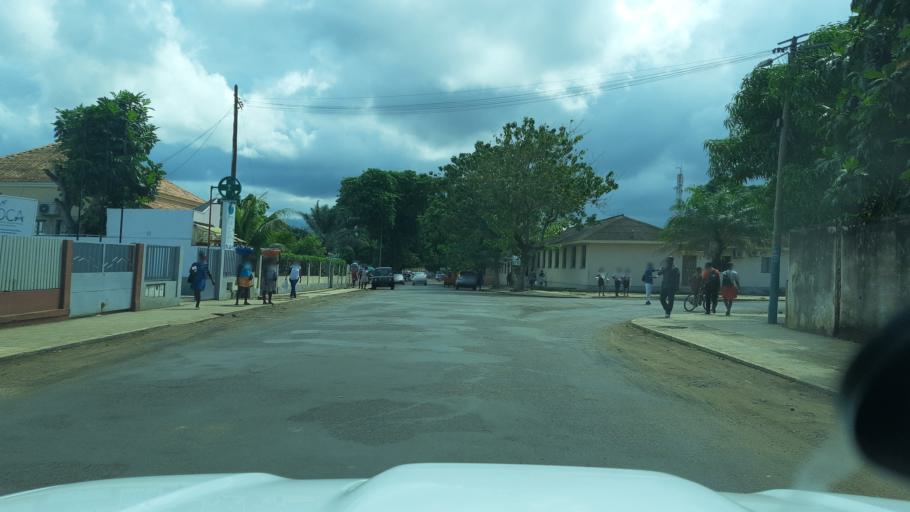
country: ST
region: Sao Tome Island
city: Sao Tome
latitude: 0.3369
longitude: 6.7339
